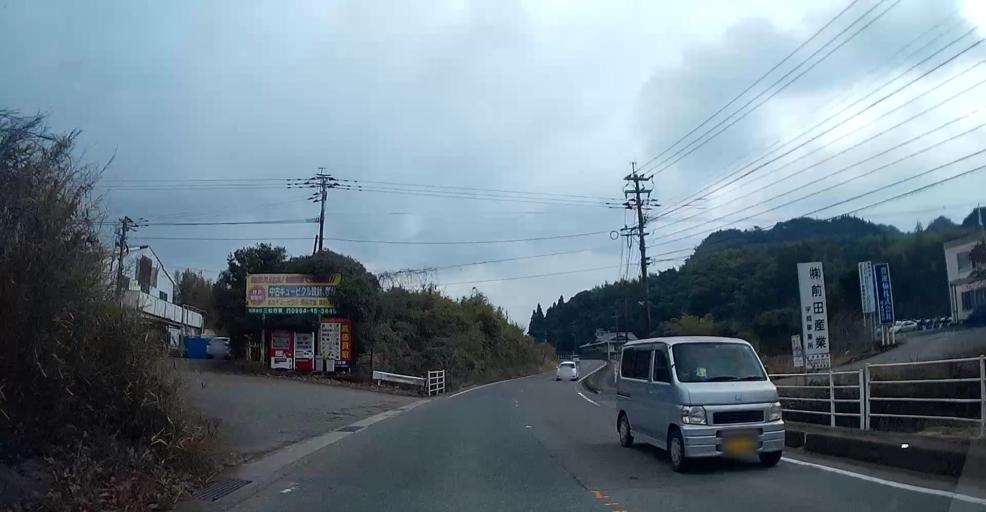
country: JP
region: Kumamoto
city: Matsubase
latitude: 32.6463
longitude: 130.7280
